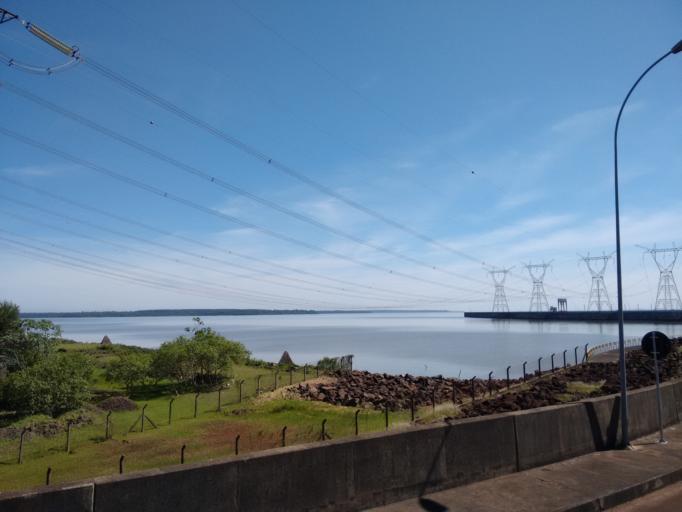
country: PY
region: Alto Parana
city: Ciudad del Este
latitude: -25.4151
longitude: -54.6016
